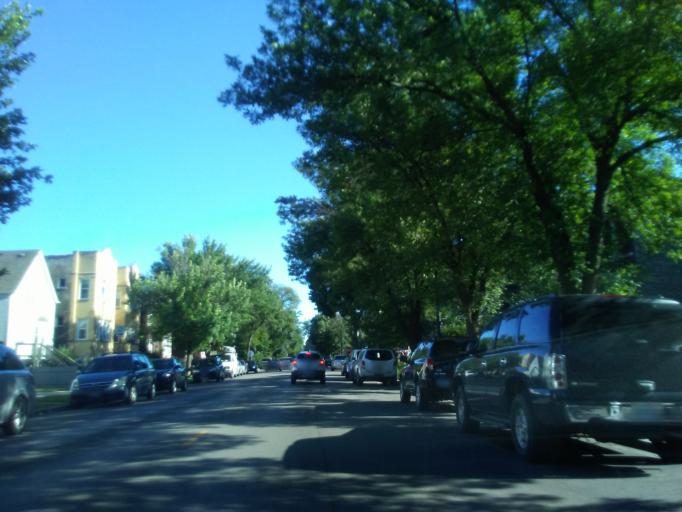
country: US
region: Illinois
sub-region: Cook County
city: Oak Park
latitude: 41.9197
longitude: -87.7365
